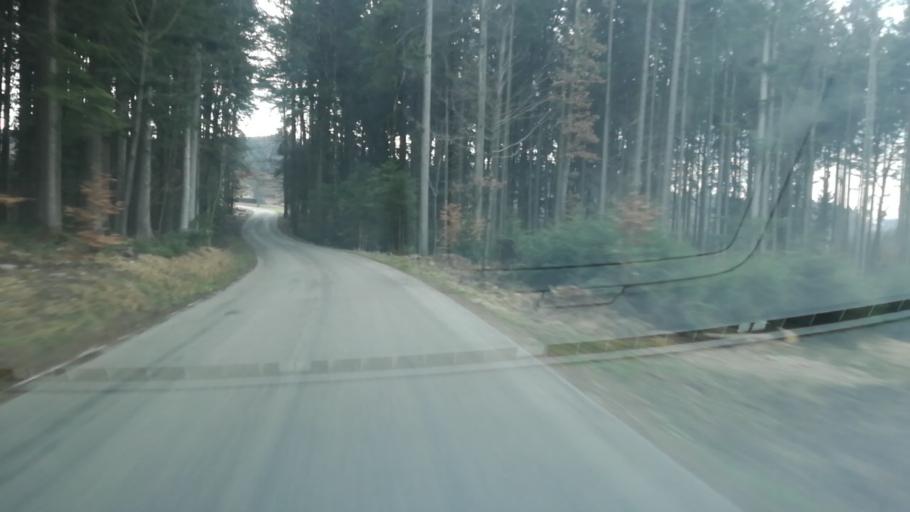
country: AT
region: Upper Austria
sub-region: Politischer Bezirk Vocklabruck
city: Neukirchen an der Vockla
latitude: 48.0571
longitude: 13.5272
